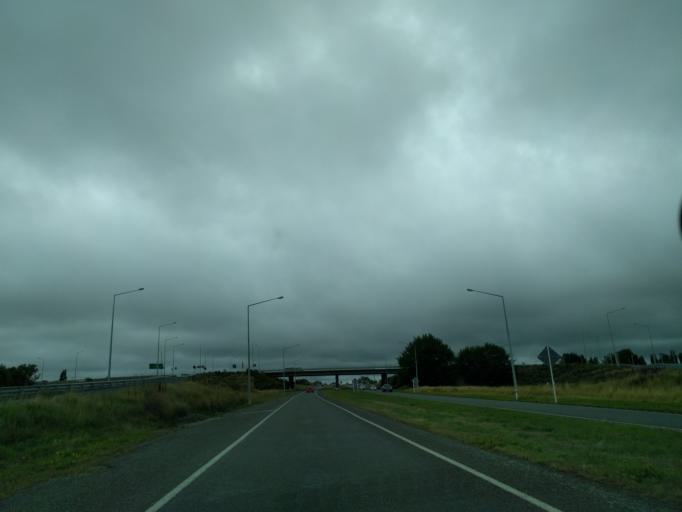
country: NZ
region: Canterbury
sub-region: Waimakariri District
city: Kaiapoi
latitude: -43.3727
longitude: 172.6476
